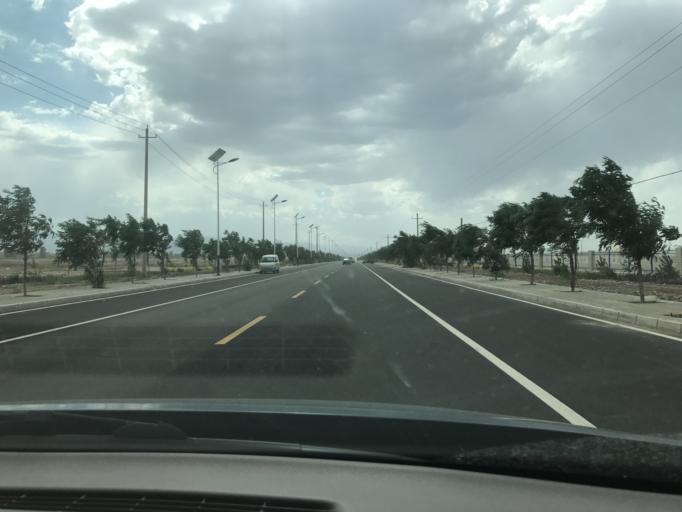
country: CN
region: Gansu Sheng
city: Wuwei
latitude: 38.1031
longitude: 102.4461
